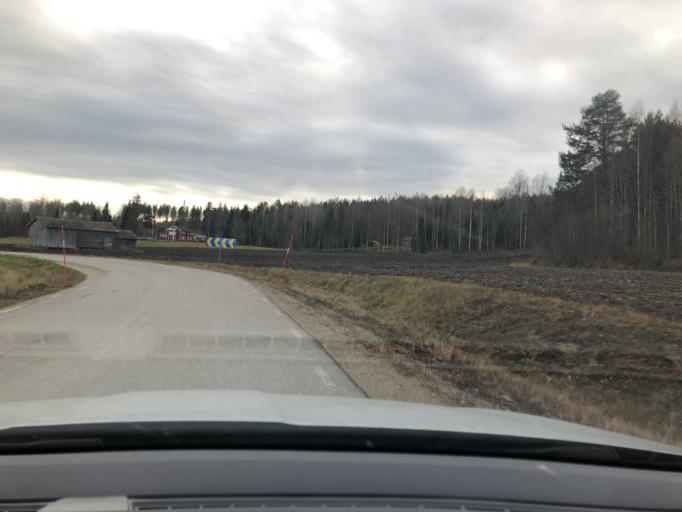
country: SE
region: Gaevleborg
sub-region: Hudiksvalls Kommun
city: Sorforsa
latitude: 61.6610
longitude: 16.9257
